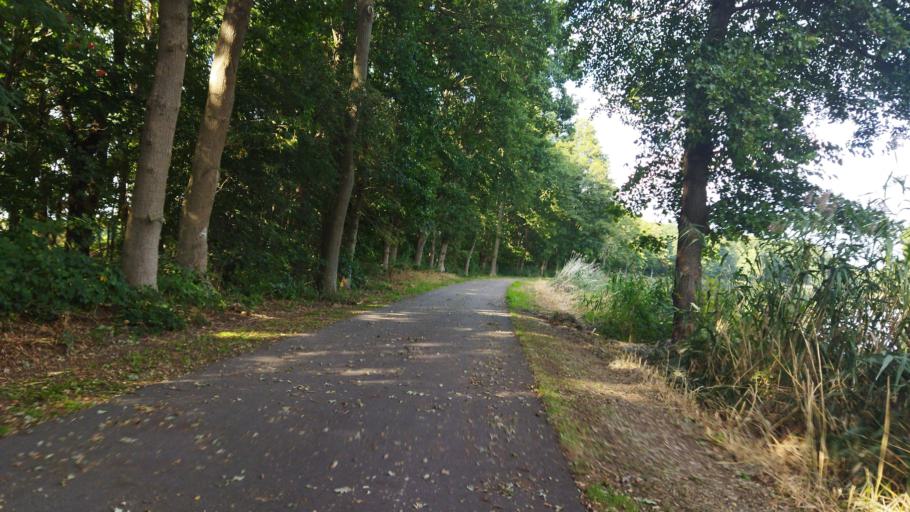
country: DE
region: Lower Saxony
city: Walchum
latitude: 52.9324
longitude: 7.2897
